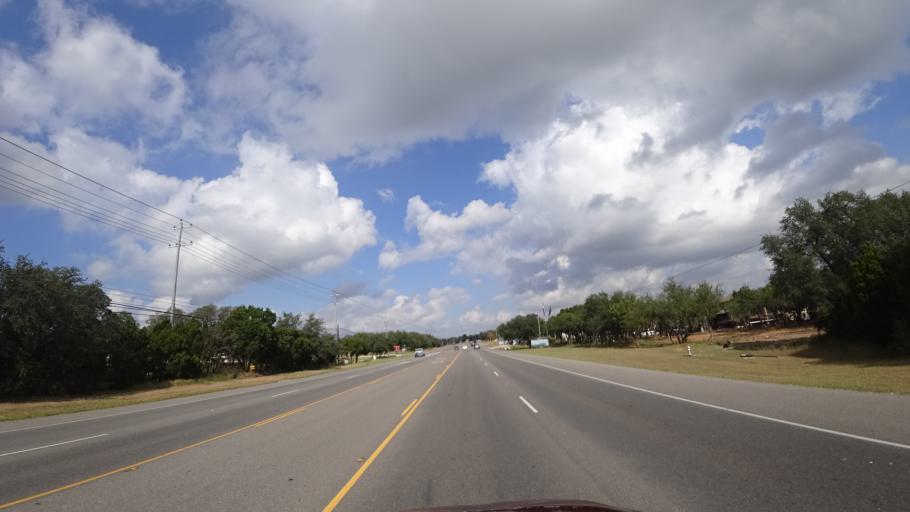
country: US
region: Texas
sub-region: Williamson County
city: Anderson Mill
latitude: 30.4311
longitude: -97.8418
